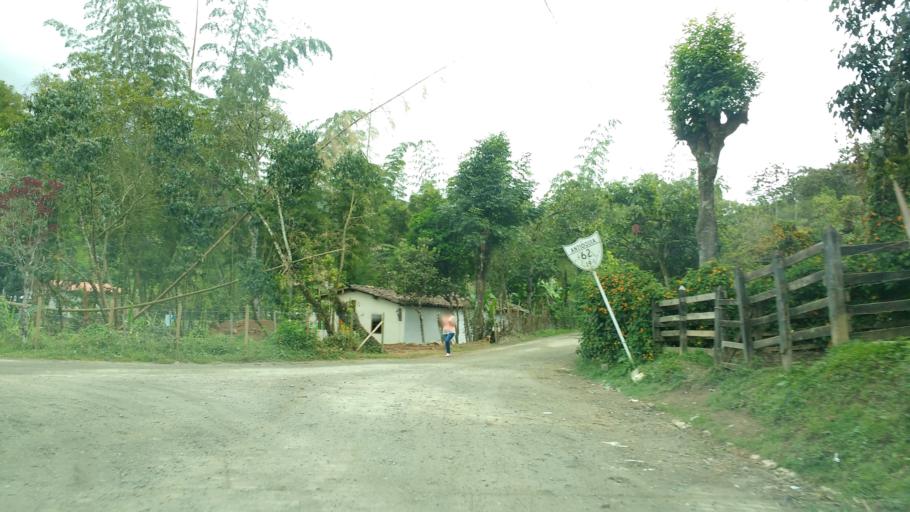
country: CO
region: Antioquia
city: Concepcion
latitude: 6.3939
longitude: -75.2538
